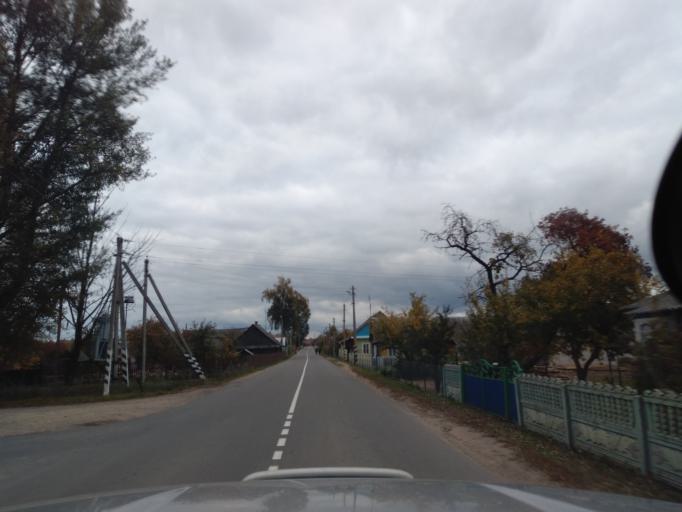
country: BY
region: Minsk
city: Kapyl'
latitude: 53.1712
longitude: 27.3314
